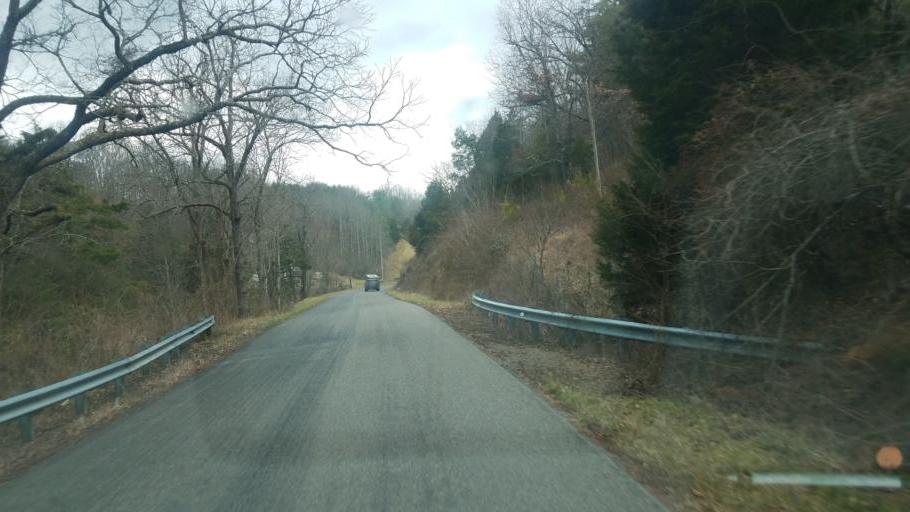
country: US
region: Virginia
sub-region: Giles County
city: Pearisburg
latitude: 37.2331
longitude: -80.6960
